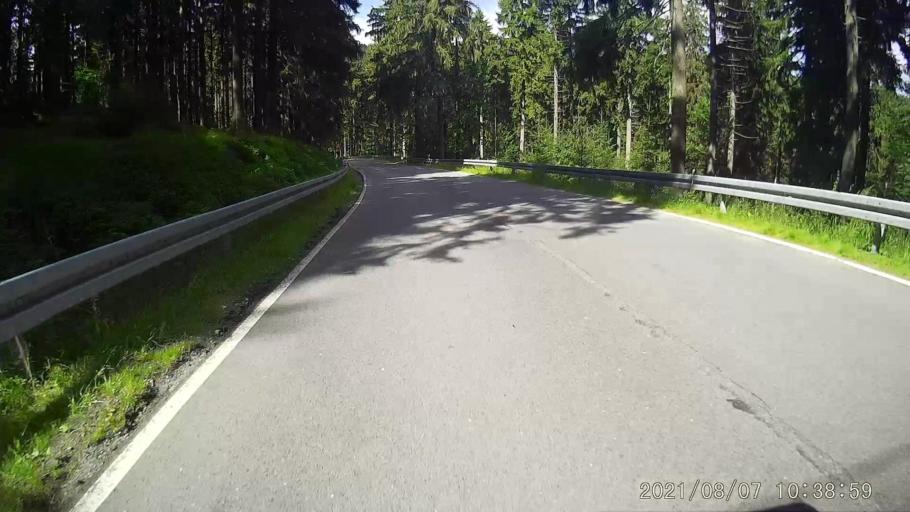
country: PL
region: Lower Silesian Voivodeship
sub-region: Powiat klodzki
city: Duszniki-Zdroj
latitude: 50.3517
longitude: 16.3764
